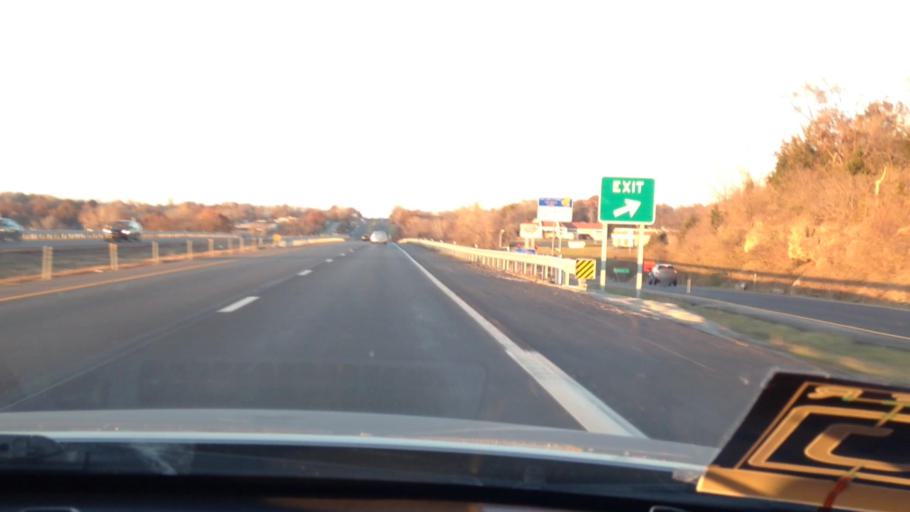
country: US
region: Missouri
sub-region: Platte County
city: Riverside
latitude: 39.1938
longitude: -94.5900
